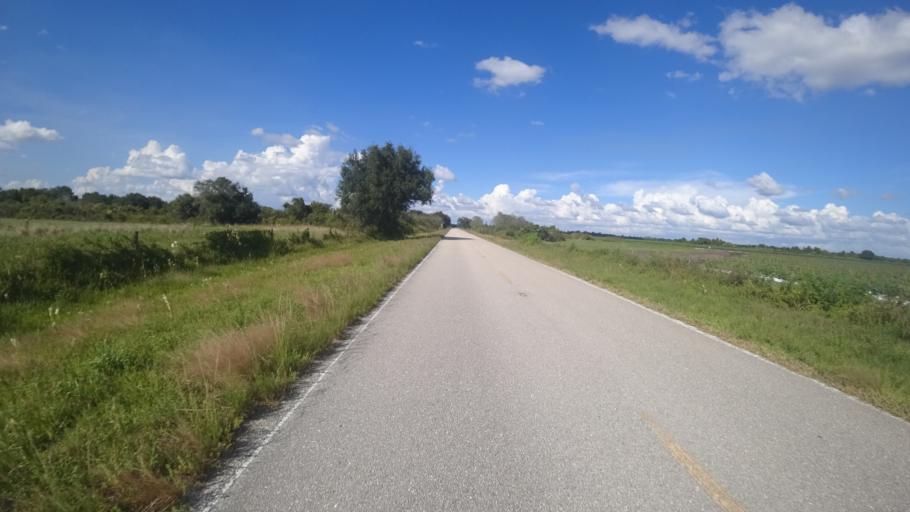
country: US
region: Florida
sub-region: DeSoto County
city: Arcadia
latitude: 27.2781
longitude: -82.0563
